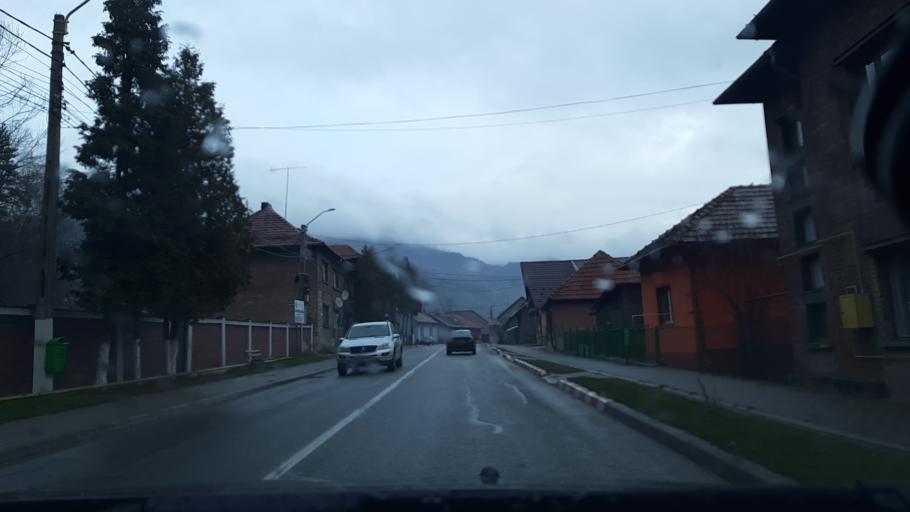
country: RO
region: Hunedoara
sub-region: Municipiul Petrosani
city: Petrosani
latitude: 45.4398
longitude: 23.3695
